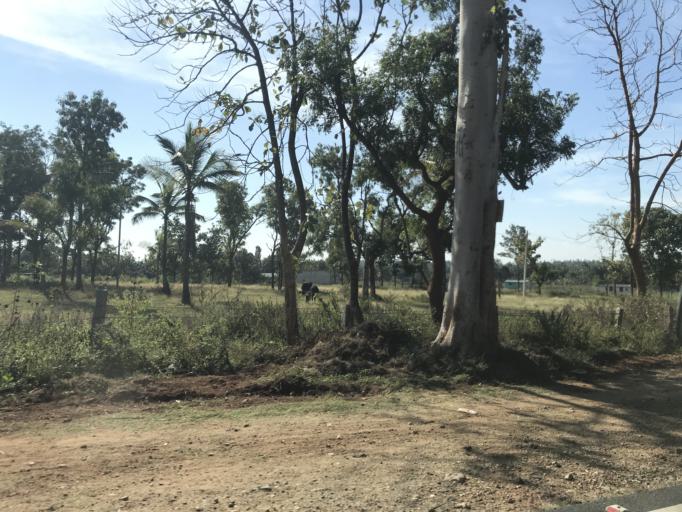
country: IN
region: Karnataka
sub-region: Mysore
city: Mysore
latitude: 12.1992
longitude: 76.5497
